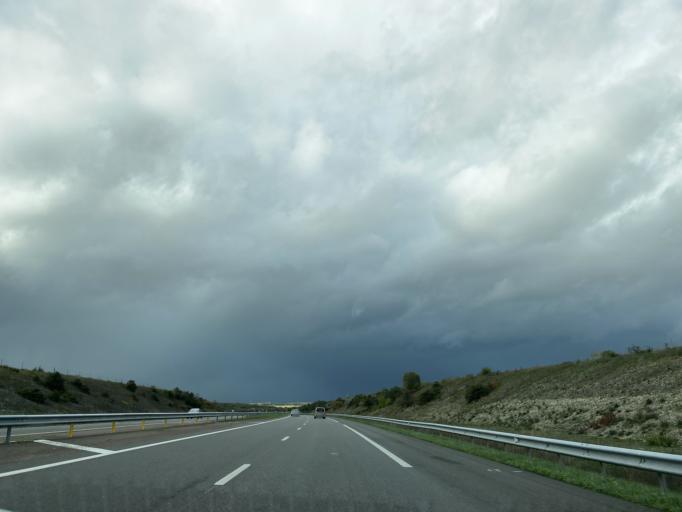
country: FR
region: Centre
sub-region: Departement du Cher
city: Trouy
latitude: 46.9980
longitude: 2.4058
